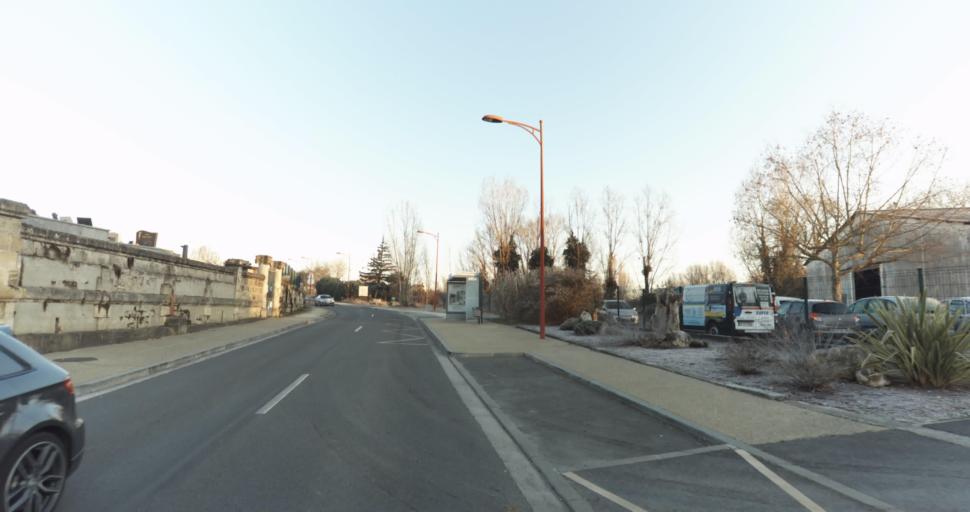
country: FR
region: Aquitaine
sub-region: Departement de la Gironde
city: Carbon-Blanc
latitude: 44.9021
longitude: -0.4968
